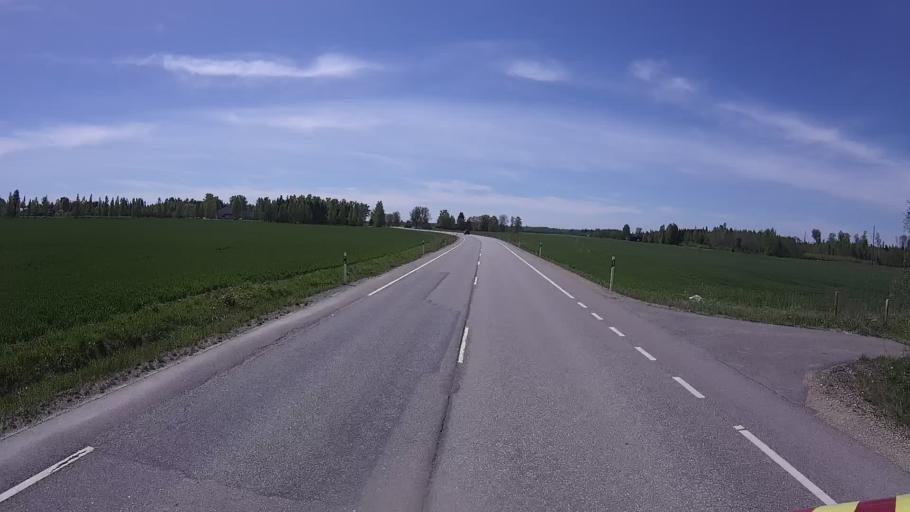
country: EE
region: Vorumaa
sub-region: Voru linn
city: Voru
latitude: 57.8695
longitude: 27.1077
